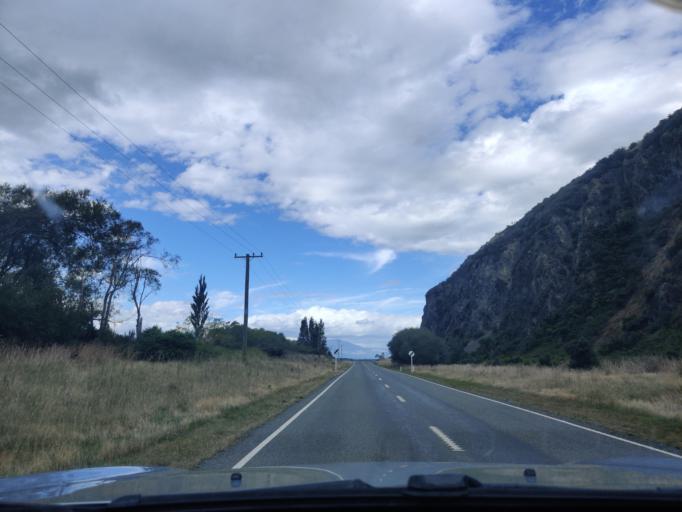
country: NZ
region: Canterbury
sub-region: Hurunui District
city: Amberley
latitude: -42.5705
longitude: 172.6800
